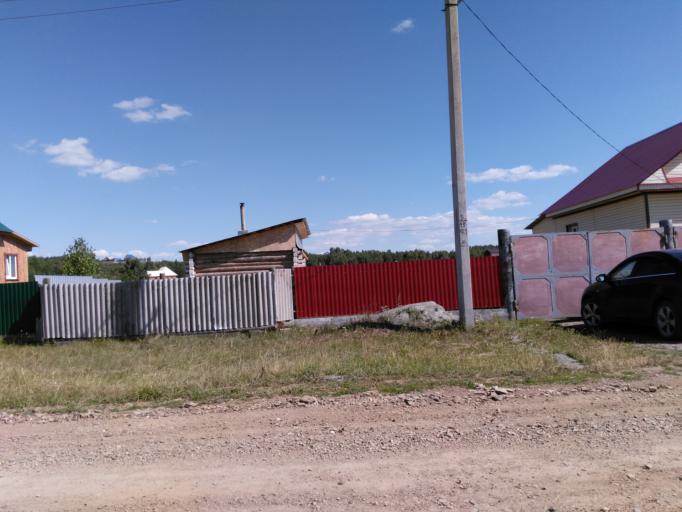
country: RU
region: Bashkortostan
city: Uchaly
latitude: 54.2911
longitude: 59.3649
